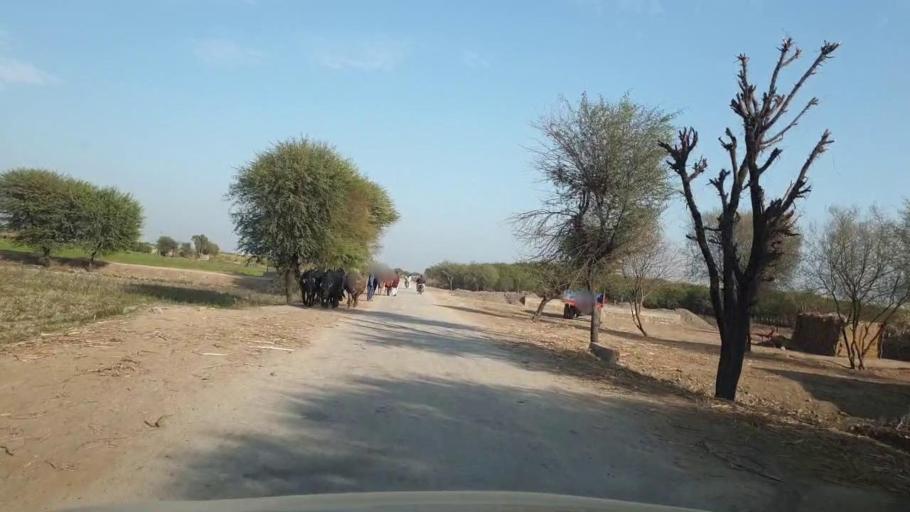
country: PK
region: Sindh
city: Tando Allahyar
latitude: 25.5936
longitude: 68.6775
